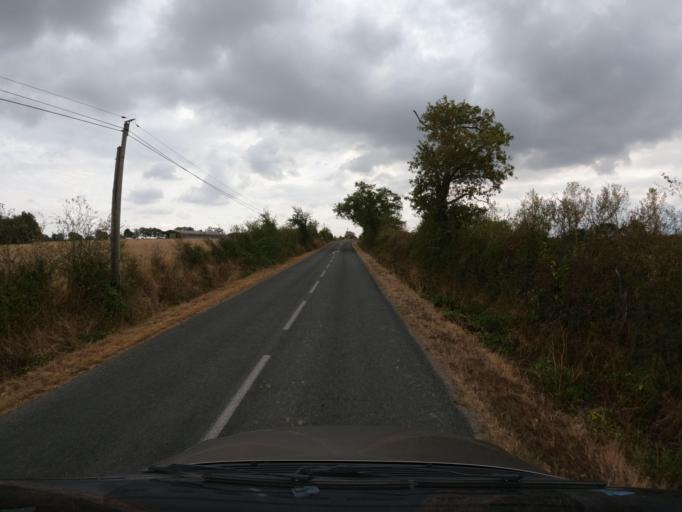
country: FR
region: Pays de la Loire
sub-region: Departement de Maine-et-Loire
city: Le Longeron
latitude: 46.9996
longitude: -1.0641
